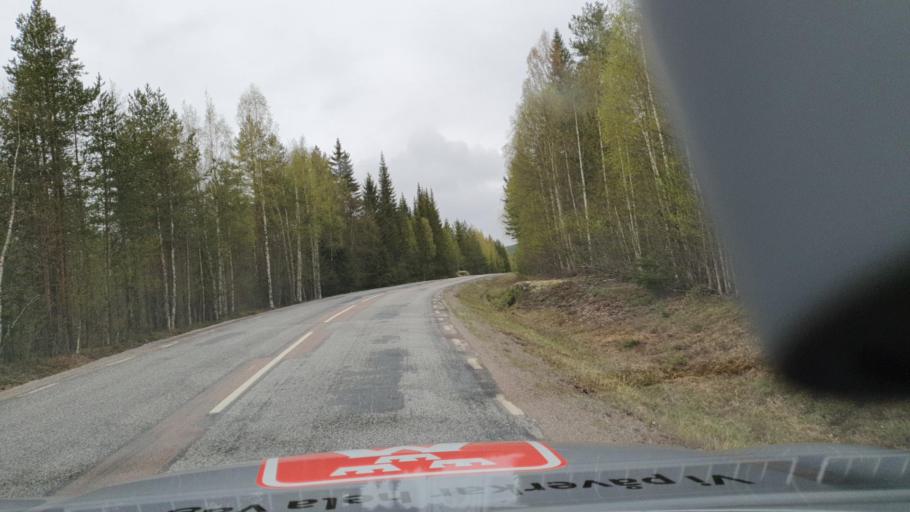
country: SE
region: Vaesternorrland
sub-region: Solleftea Kommun
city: Solleftea
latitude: 63.6686
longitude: 17.2564
